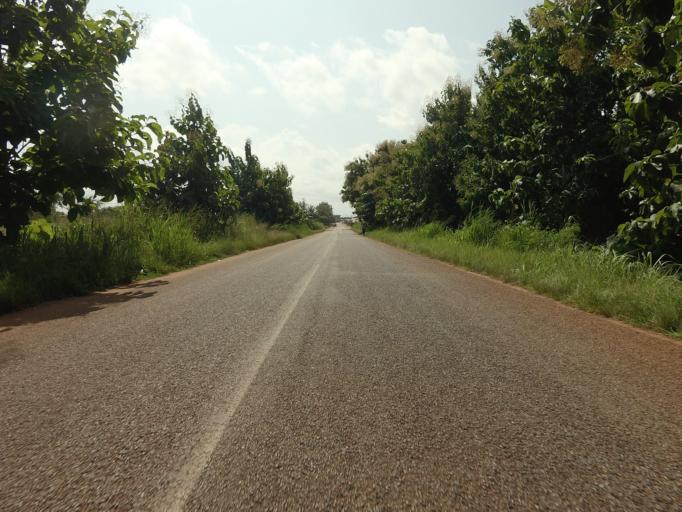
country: TG
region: Maritime
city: Tsevie
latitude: 6.3577
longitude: 0.8675
